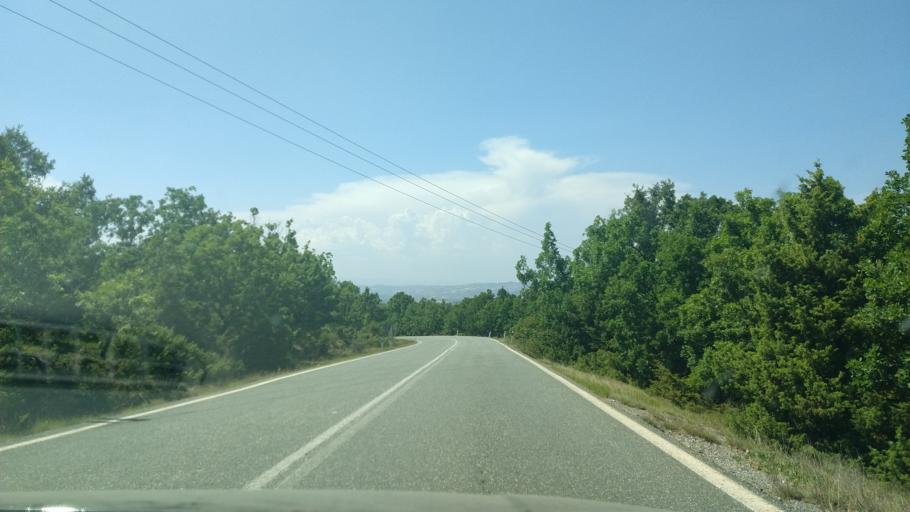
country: GR
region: West Macedonia
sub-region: Nomos Grevenon
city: Grevena
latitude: 40.0204
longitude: 21.4872
